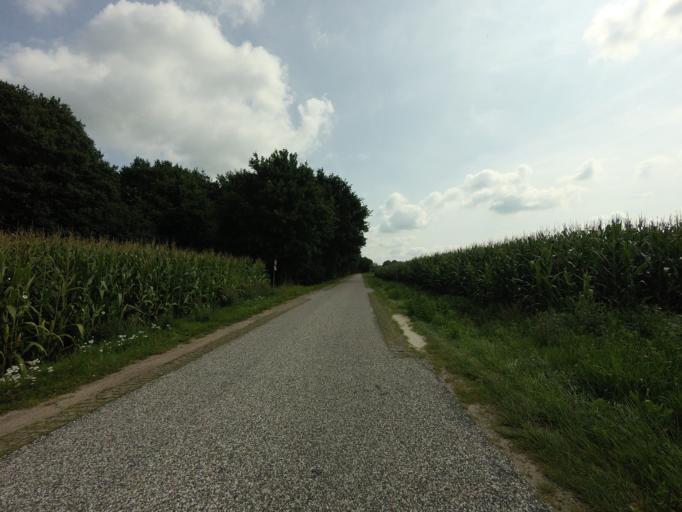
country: NL
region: Overijssel
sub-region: Gemeente Tubbergen
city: Tubbergen
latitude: 52.4126
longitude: 6.8387
